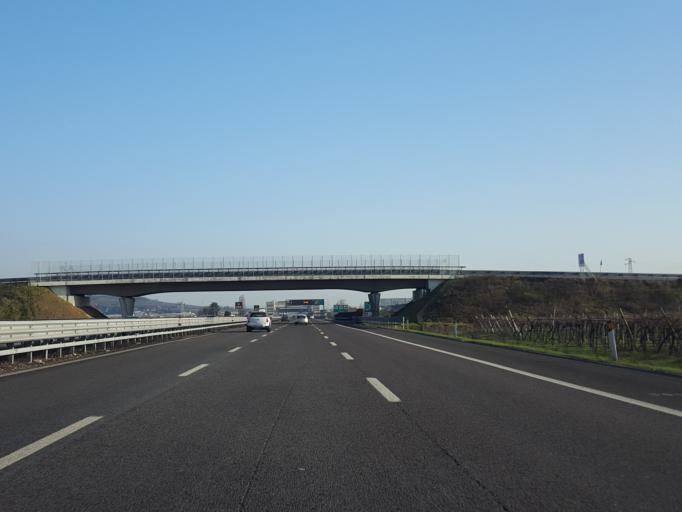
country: IT
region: Veneto
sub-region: Provincia di Verona
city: Soave
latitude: 45.4122
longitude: 11.2206
